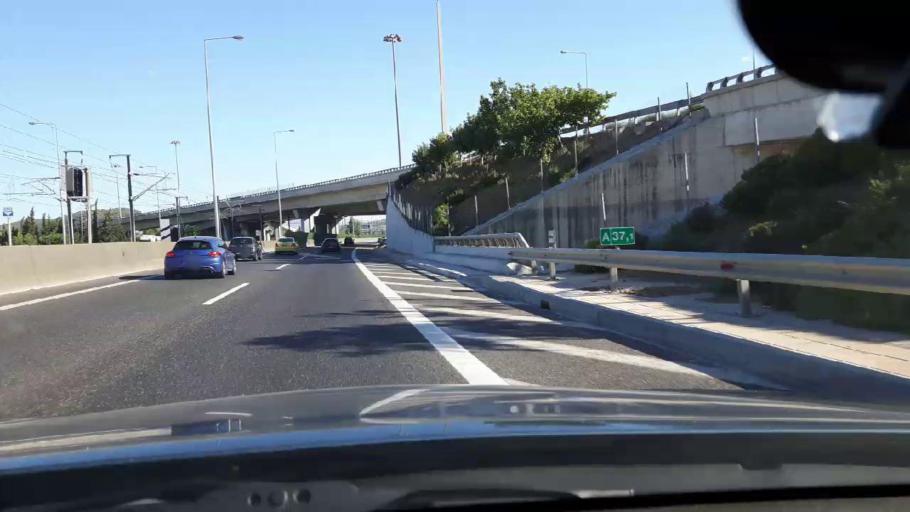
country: GR
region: Attica
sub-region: Nomarchia Anatolikis Attikis
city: Pallini
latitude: 37.9850
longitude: 23.8699
